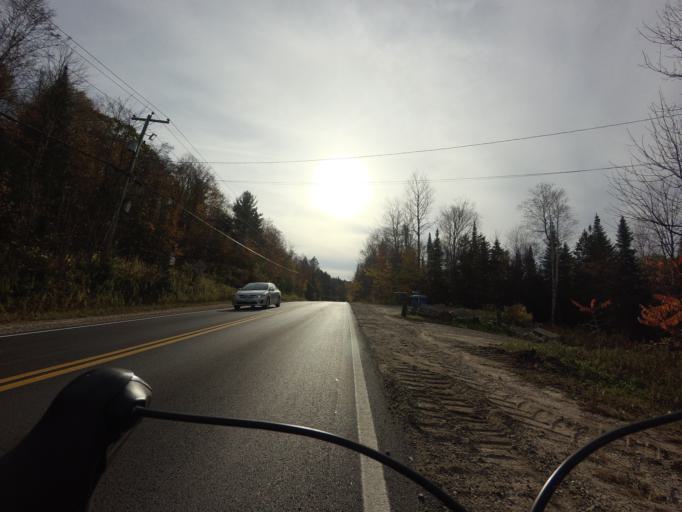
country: CA
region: Quebec
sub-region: Outaouais
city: Wakefield
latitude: 45.6517
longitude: -75.7581
